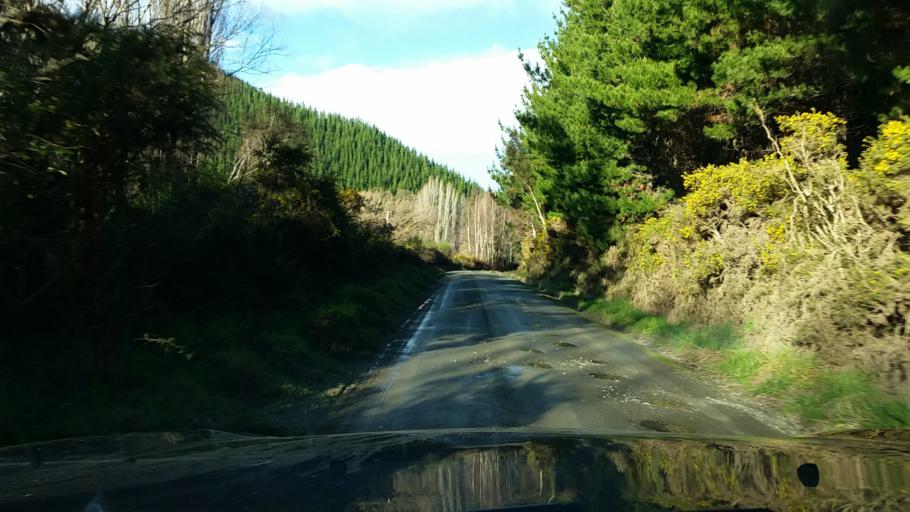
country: NZ
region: Nelson
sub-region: Nelson City
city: Nelson
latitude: -41.5553
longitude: 173.4274
